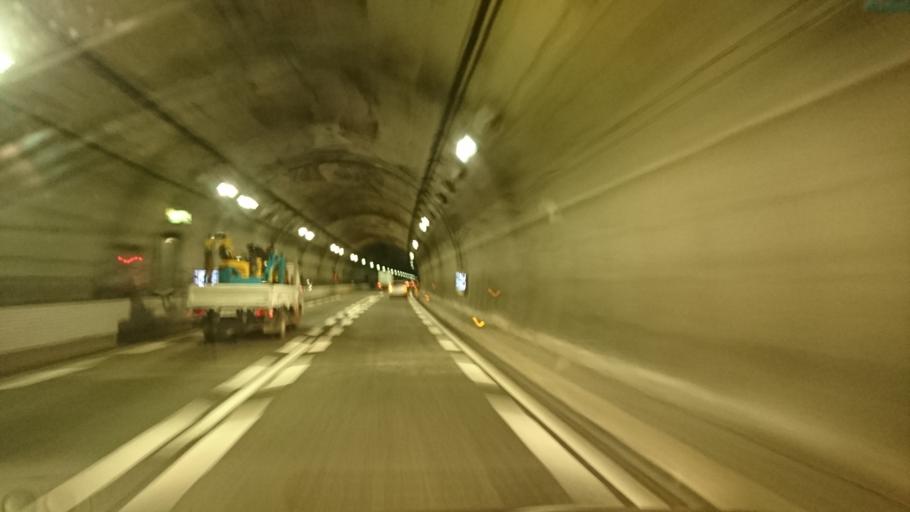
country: JP
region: Okayama
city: Okayama-shi
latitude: 34.7309
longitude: 133.9777
